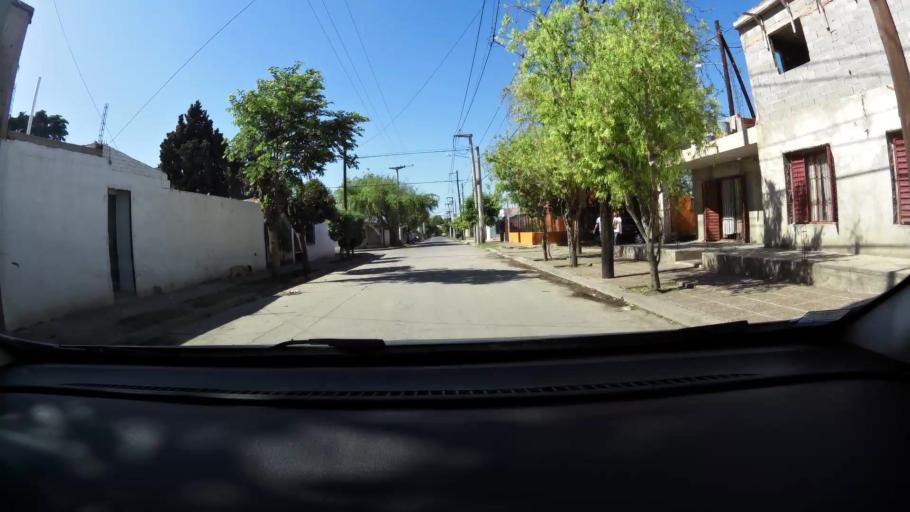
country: AR
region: Cordoba
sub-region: Departamento de Capital
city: Cordoba
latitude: -31.4422
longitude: -64.1420
